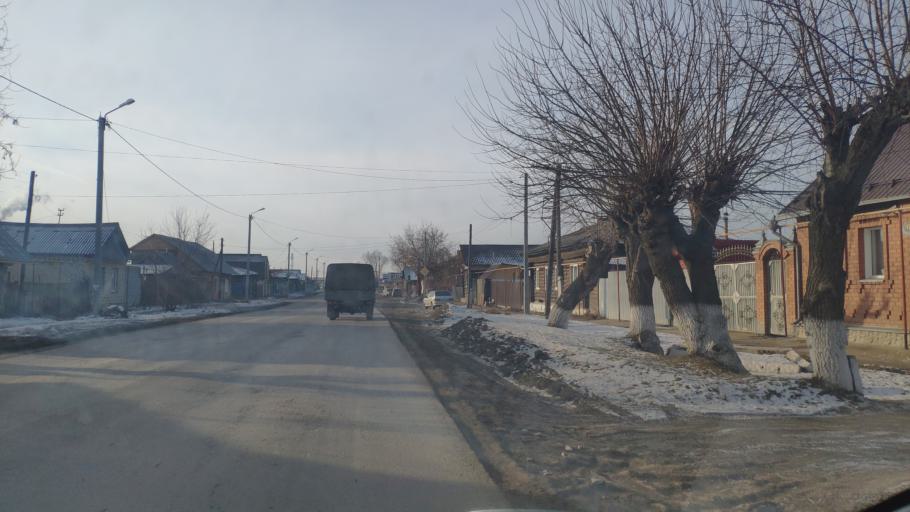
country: RU
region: Kurgan
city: Shadrinsk
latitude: 56.0903
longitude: 63.6808
